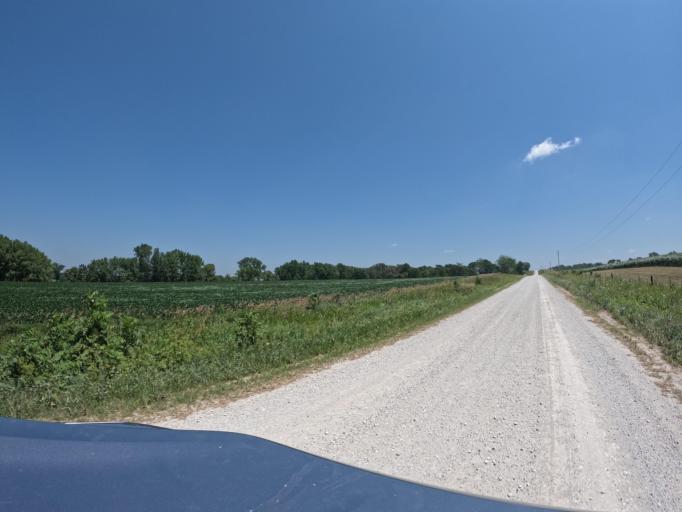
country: US
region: Iowa
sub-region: Keokuk County
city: Sigourney
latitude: 41.2869
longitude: -92.1700
